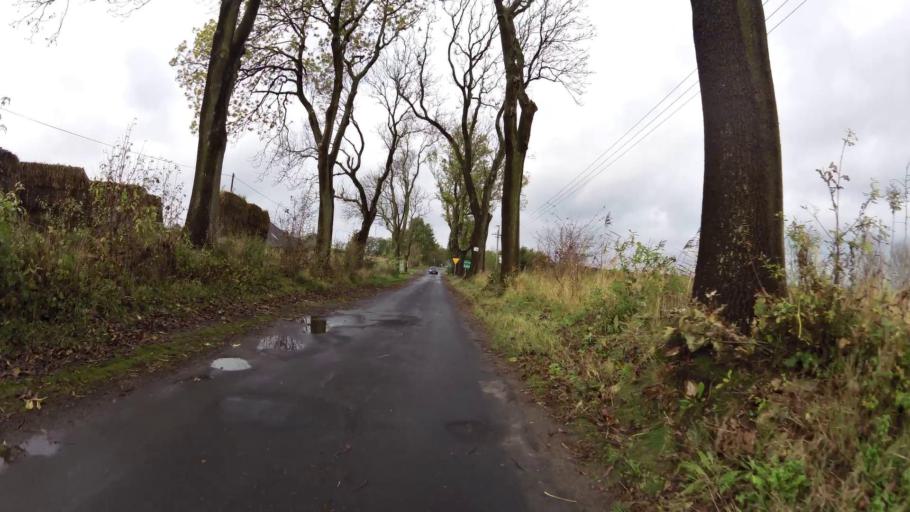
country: PL
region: West Pomeranian Voivodeship
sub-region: Powiat gryfinski
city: Gryfino
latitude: 53.2331
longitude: 14.5195
